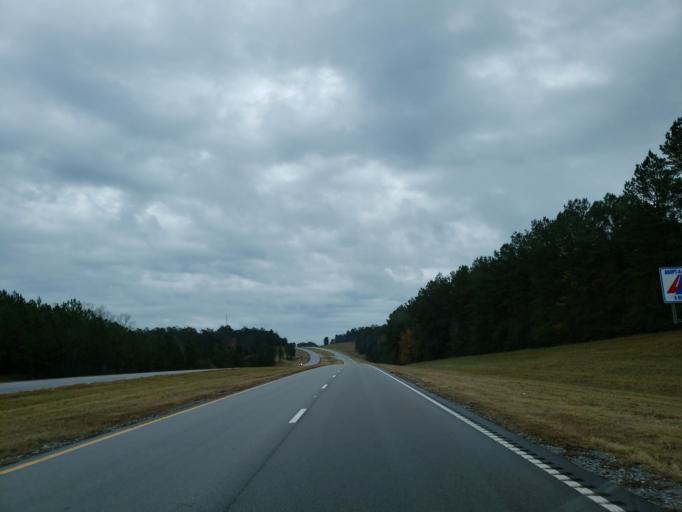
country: US
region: Mississippi
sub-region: Wayne County
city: Waynesboro
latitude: 31.6873
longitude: -88.7048
